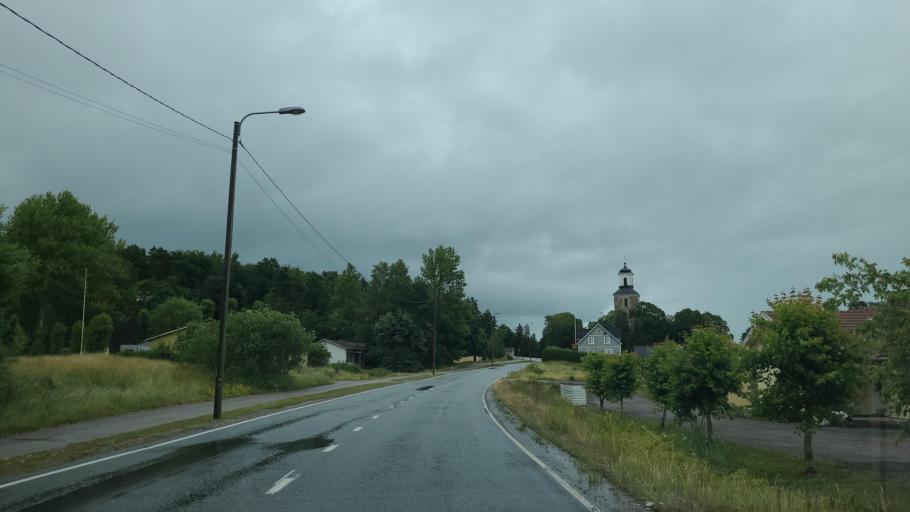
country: FI
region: Varsinais-Suomi
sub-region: Aboland-Turunmaa
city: Kimito
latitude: 60.1681
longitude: 22.7401
